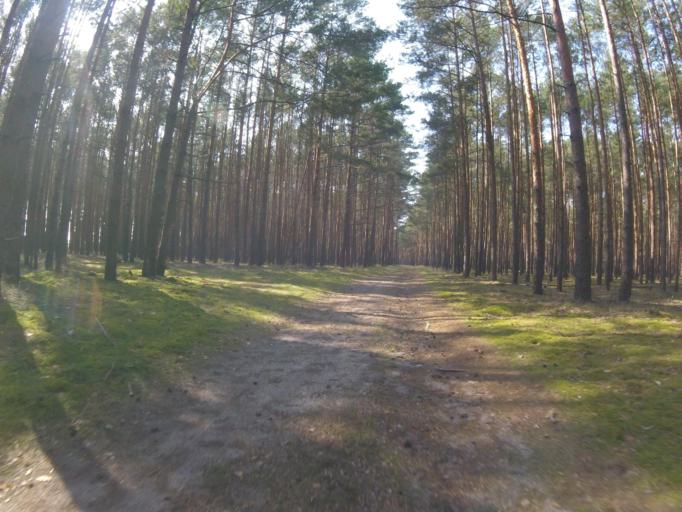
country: DE
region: Brandenburg
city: Bestensee
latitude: 52.2553
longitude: 13.7613
